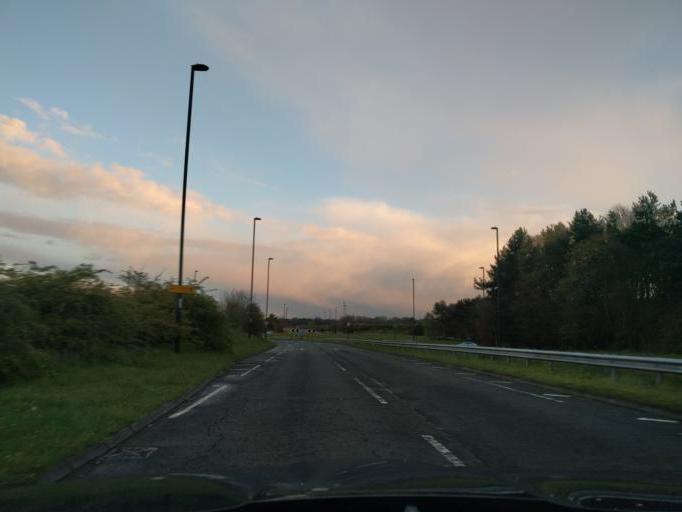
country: GB
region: England
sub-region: Northumberland
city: Cramlington
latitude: 55.0407
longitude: -1.5922
